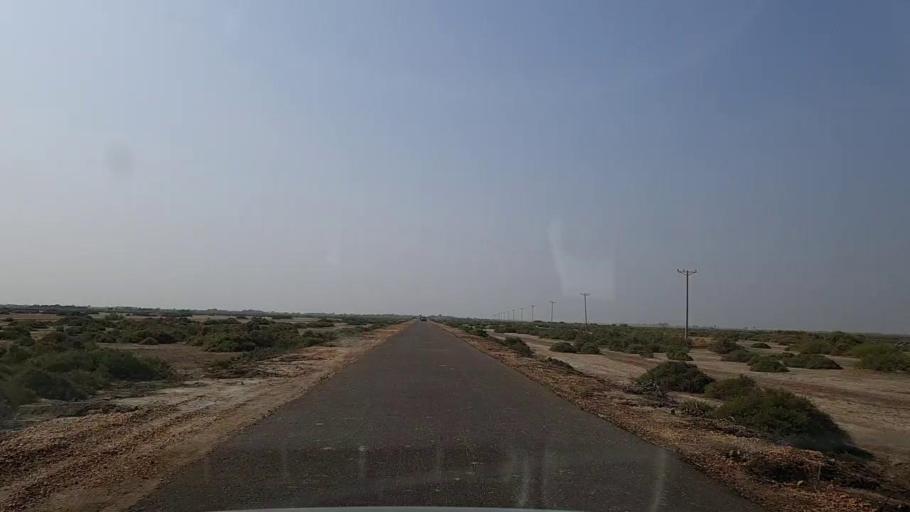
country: PK
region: Sindh
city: Mirpur Sakro
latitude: 24.5289
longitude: 67.5765
